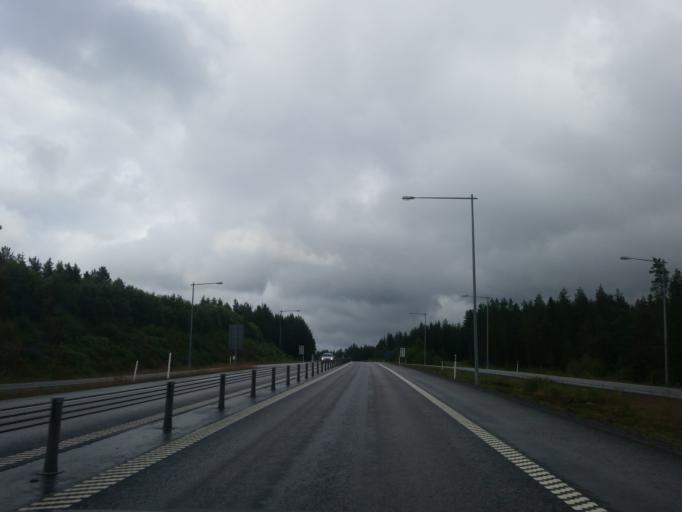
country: SE
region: Vaesterbotten
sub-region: Umea Kommun
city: Saevar
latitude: 63.8998
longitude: 20.5670
